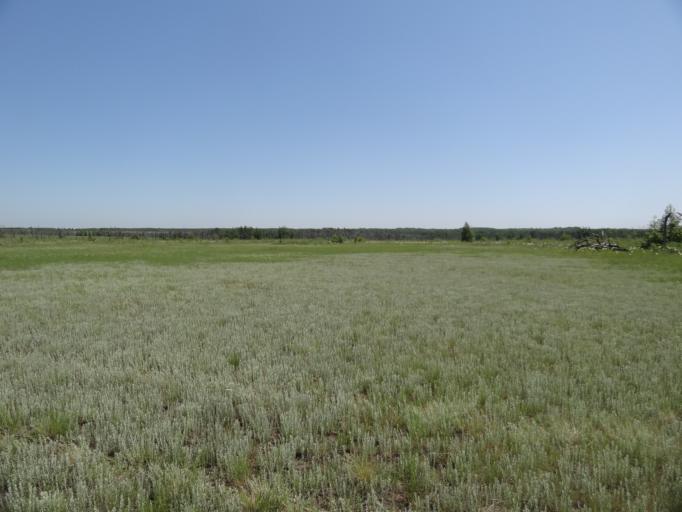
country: RU
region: Saratov
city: Krasnyy Oktyabr'
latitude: 51.2960
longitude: 45.5513
